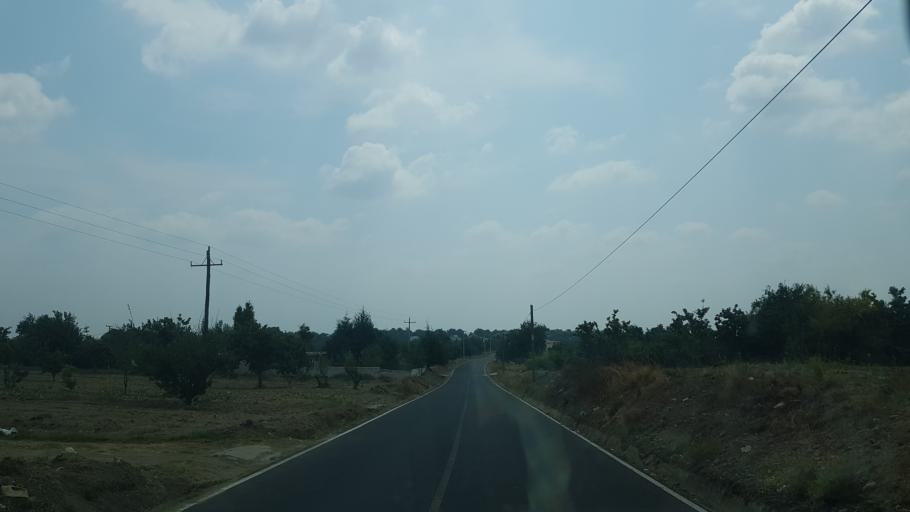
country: MX
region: Puebla
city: Domingo Arenas
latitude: 19.1420
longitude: -98.4762
